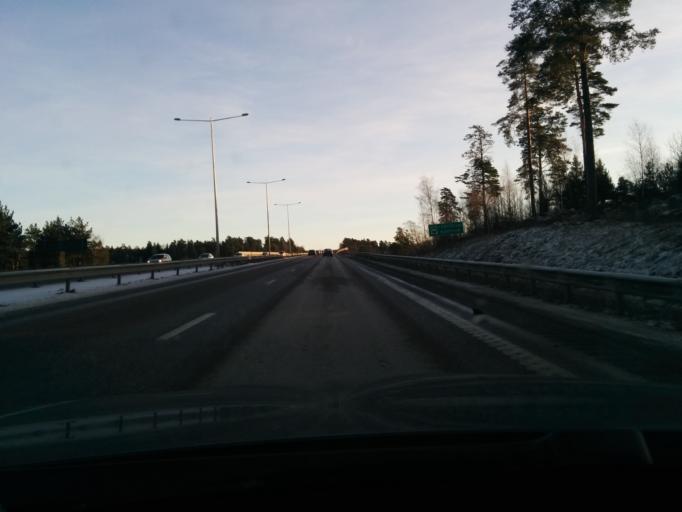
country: SE
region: Stockholm
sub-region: Upplands-Bro Kommun
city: Kungsaengen
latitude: 59.4790
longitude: 17.7885
